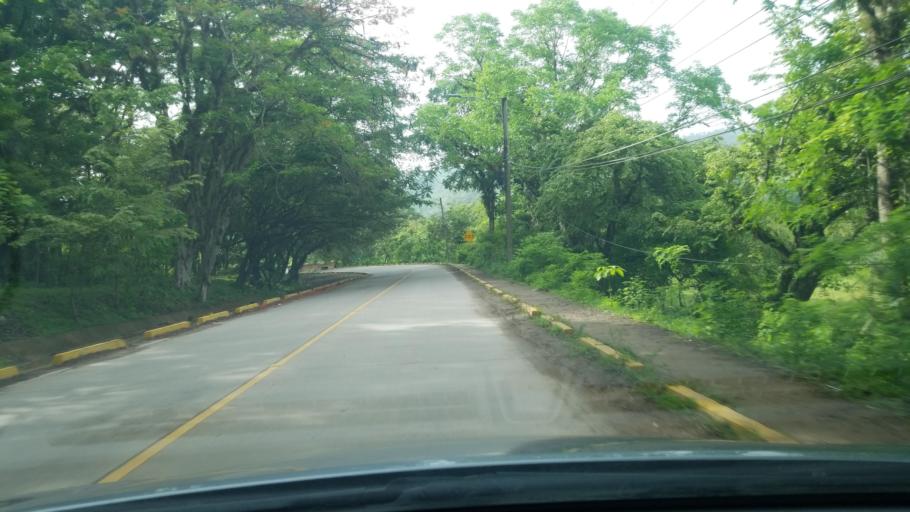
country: HN
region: Copan
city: Copan
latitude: 14.8395
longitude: -89.1517
